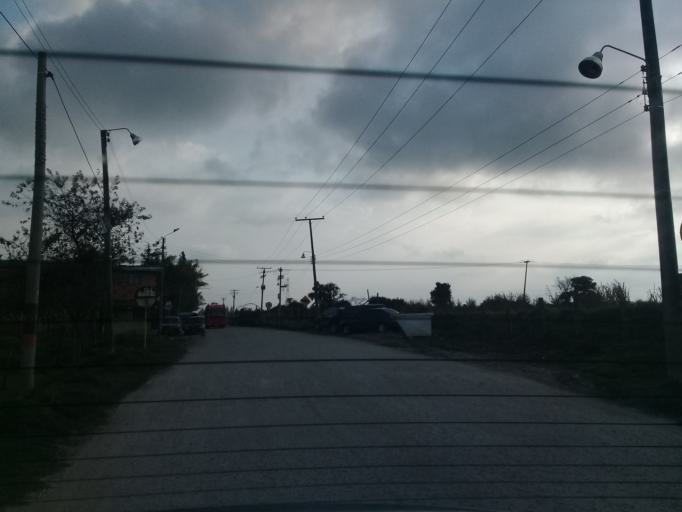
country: CO
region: Cundinamarca
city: Madrid
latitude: 4.7889
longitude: -74.2200
